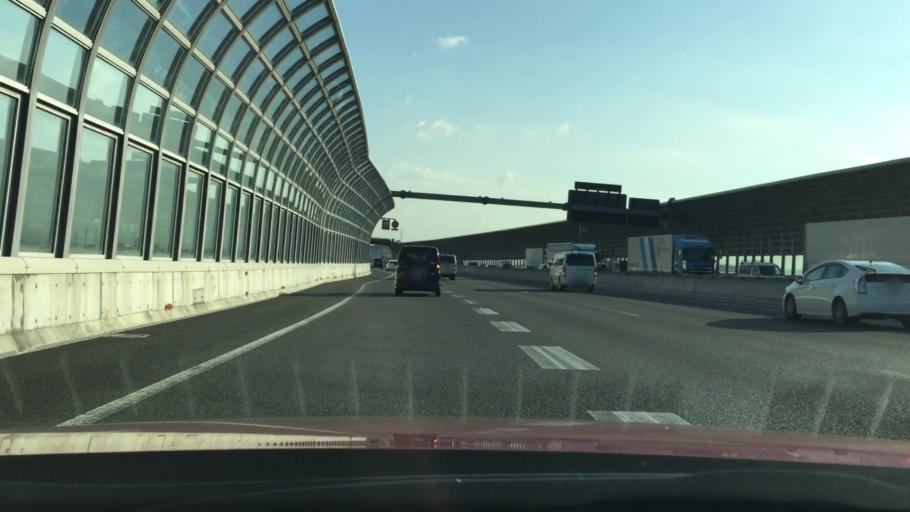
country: JP
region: Osaka
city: Daitocho
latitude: 34.7210
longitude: 135.5986
